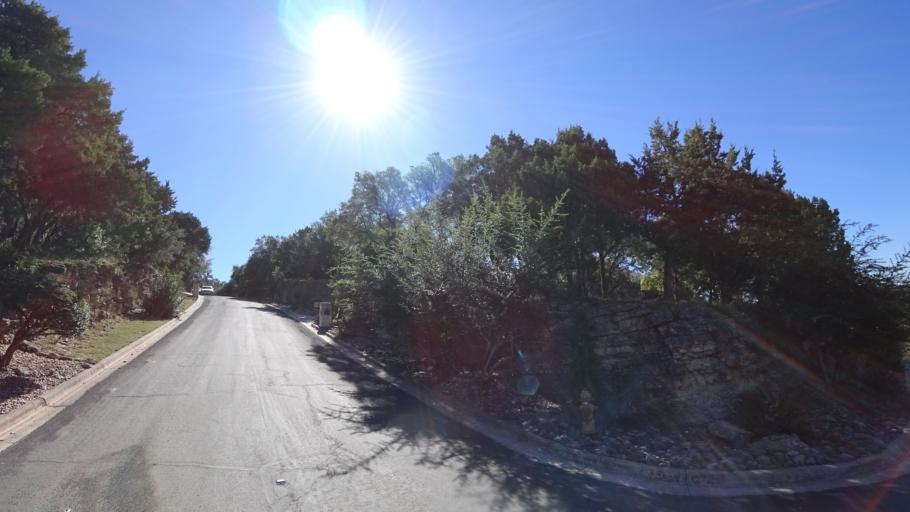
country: US
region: Texas
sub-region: Travis County
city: West Lake Hills
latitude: 30.3218
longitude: -97.7931
